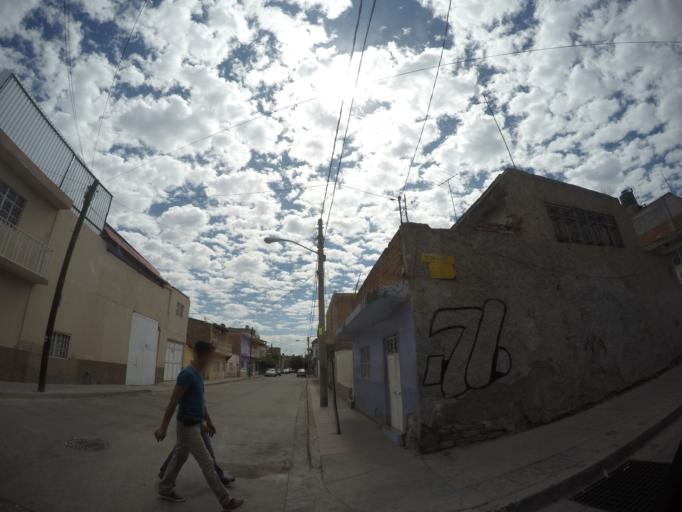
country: MX
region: Guanajuato
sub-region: Leon
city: San Jose de Duran (Los Troncoso)
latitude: 21.0933
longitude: -101.6806
